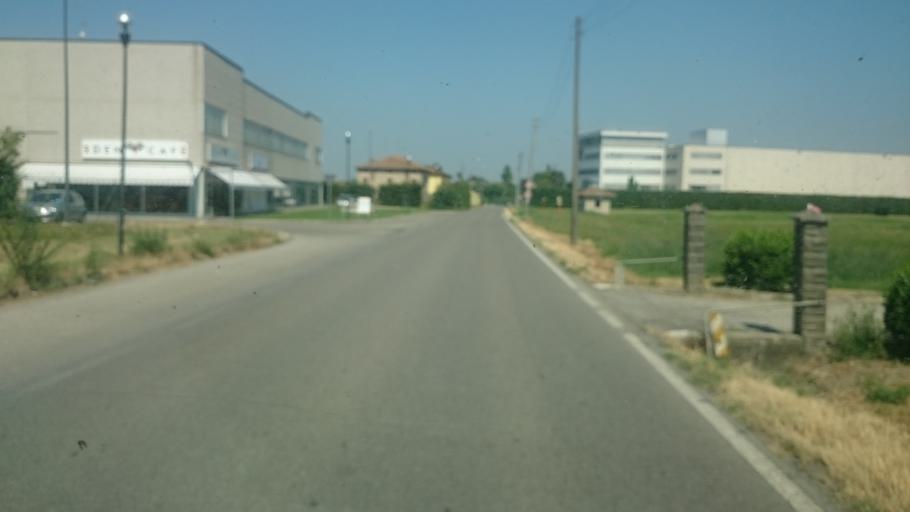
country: IT
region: Emilia-Romagna
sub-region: Provincia di Reggio Emilia
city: Fogliano
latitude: 44.6423
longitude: 10.6724
